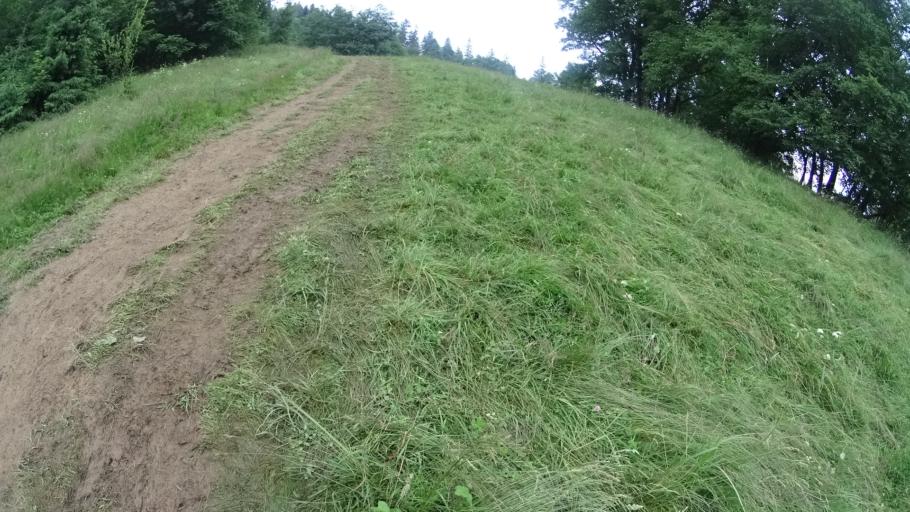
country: PL
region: Lesser Poland Voivodeship
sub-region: Powiat tatrzanski
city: Zakopane
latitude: 49.3020
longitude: 19.9404
